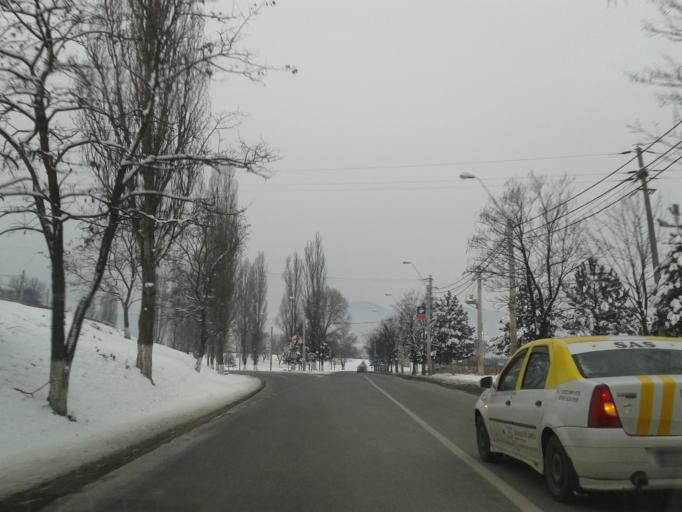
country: RO
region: Hunedoara
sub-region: Municipiul Deva
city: Cristur
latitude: 45.8605
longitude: 22.9309
